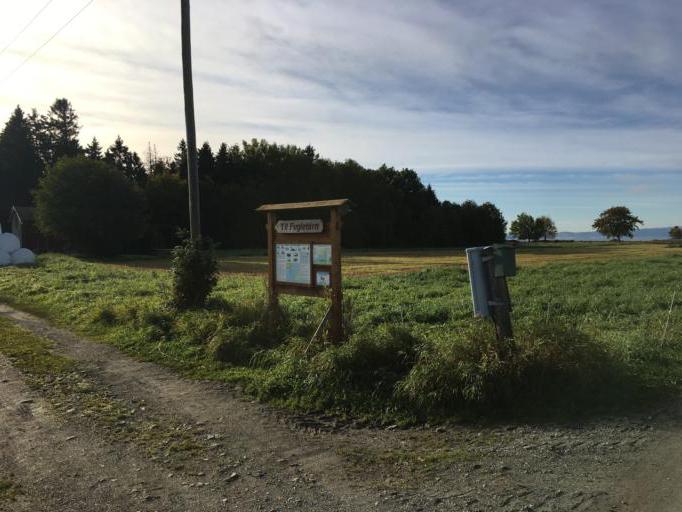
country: NO
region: Nord-Trondelag
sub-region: Leksvik
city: Leksvik
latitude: 63.5751
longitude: 10.6119
